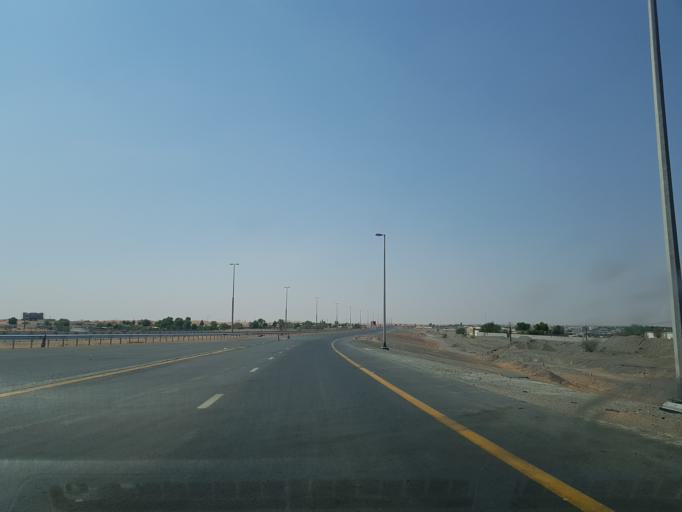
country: AE
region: Ash Shariqah
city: Adh Dhayd
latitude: 25.2325
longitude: 55.9133
